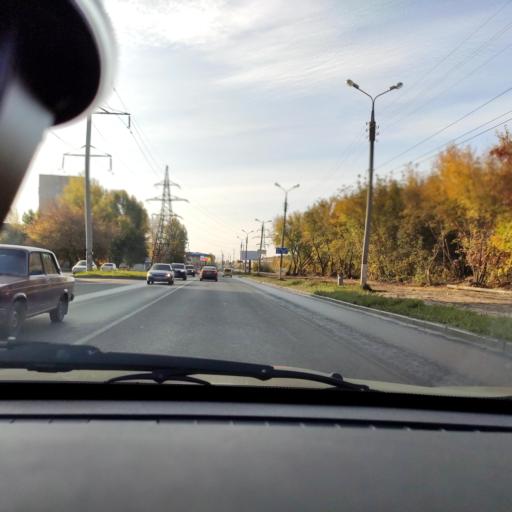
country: RU
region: Samara
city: Tol'yatti
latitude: 53.5266
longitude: 49.3963
